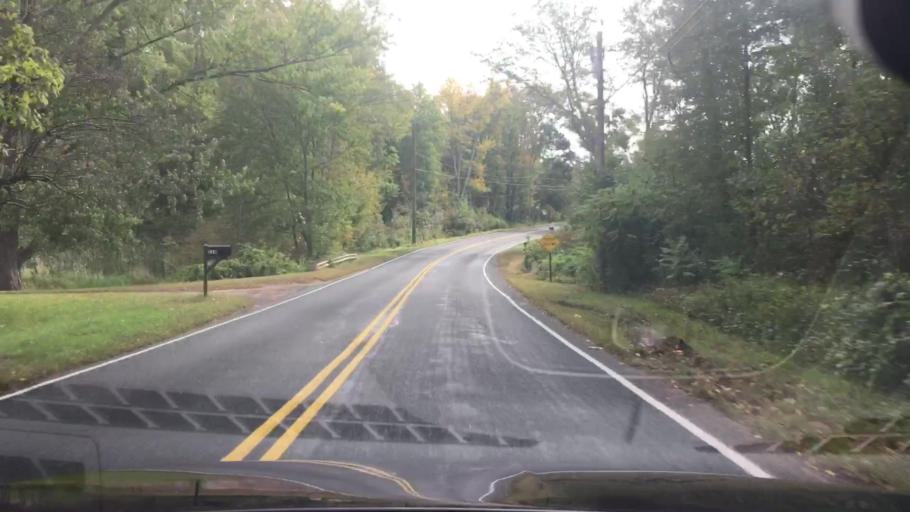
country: US
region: Connecticut
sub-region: Tolland County
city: Somers
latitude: 41.9926
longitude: -72.4943
